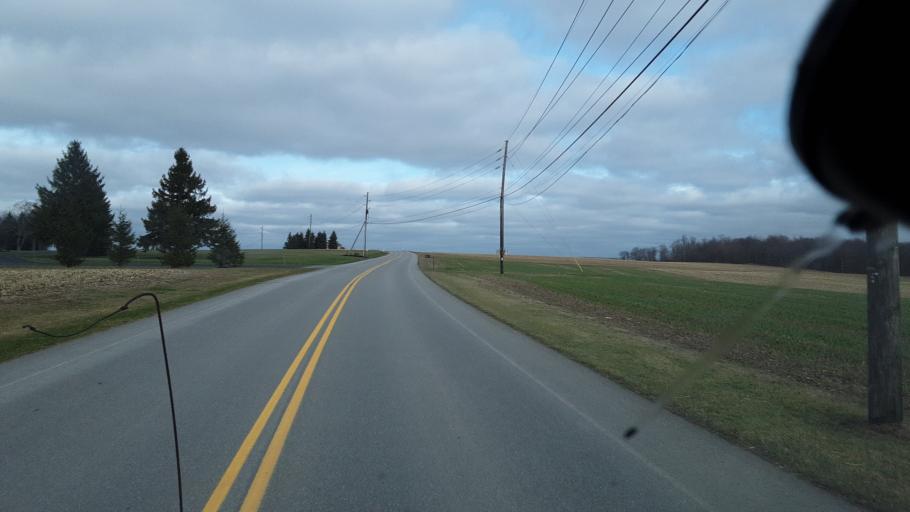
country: US
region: Pennsylvania
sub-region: Potter County
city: Galeton
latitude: 41.8765
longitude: -77.7637
